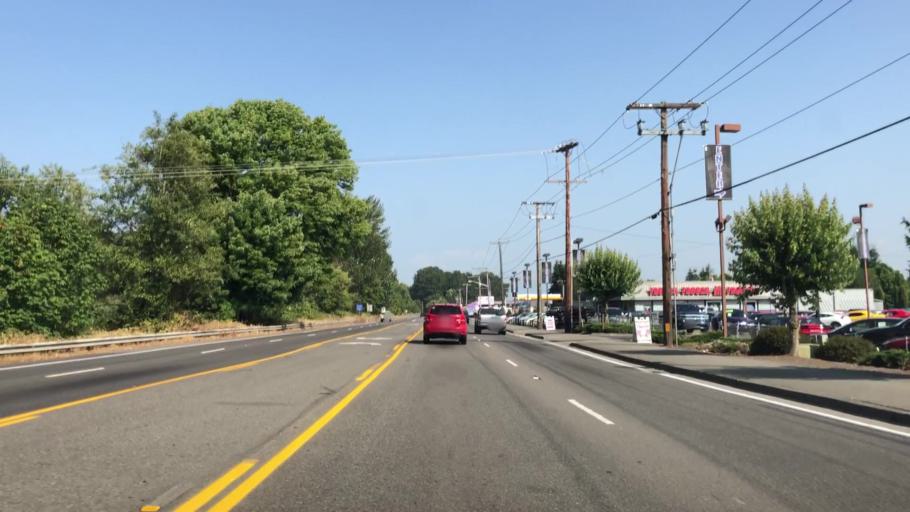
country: US
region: Washington
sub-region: Pierce County
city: Puyallup
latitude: 47.2065
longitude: -122.3209
